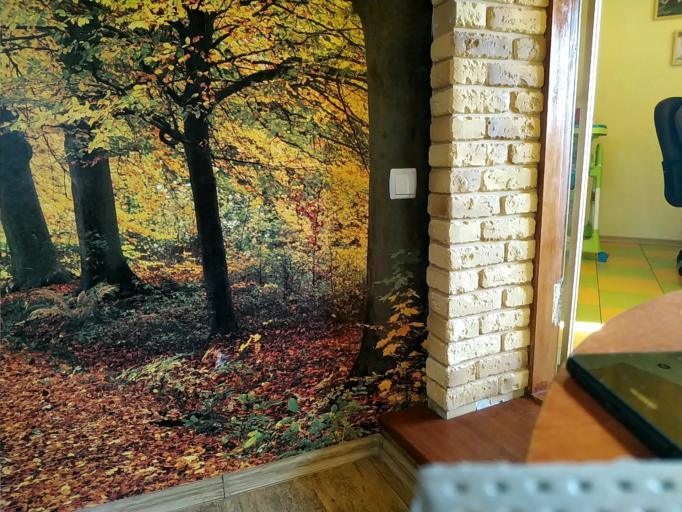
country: RU
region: Tverskaya
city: Zubtsov
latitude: 56.2047
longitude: 34.5693
